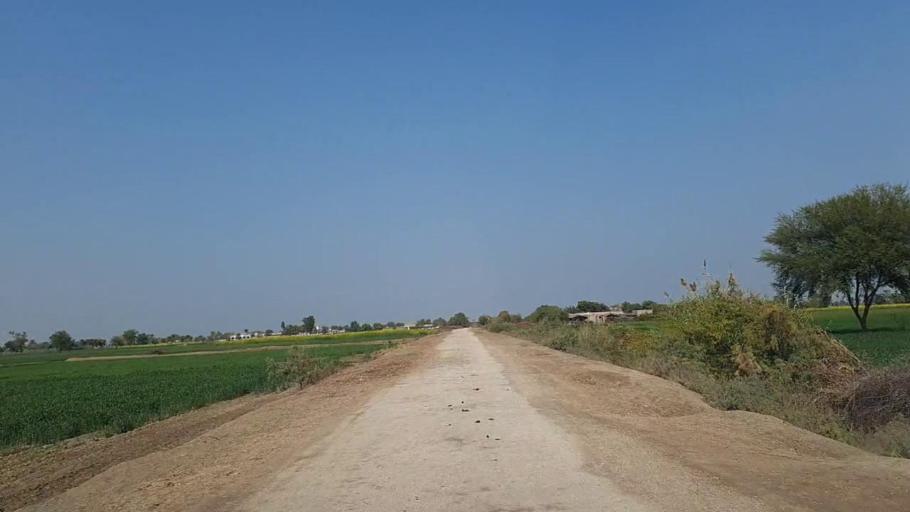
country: PK
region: Sindh
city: Nawabshah
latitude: 26.2758
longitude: 68.5135
